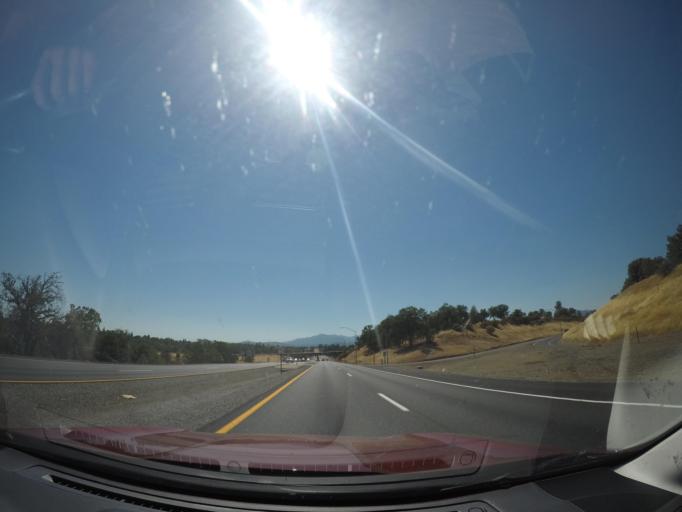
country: US
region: California
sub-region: Shasta County
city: Redding
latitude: 40.6129
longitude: -122.3601
